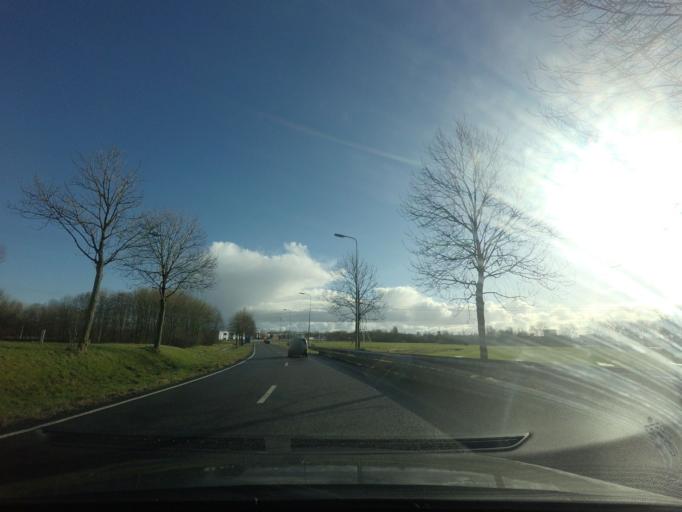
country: NL
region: Groningen
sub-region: Gemeente Groningen
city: Korrewegwijk
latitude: 53.2494
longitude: 6.5708
